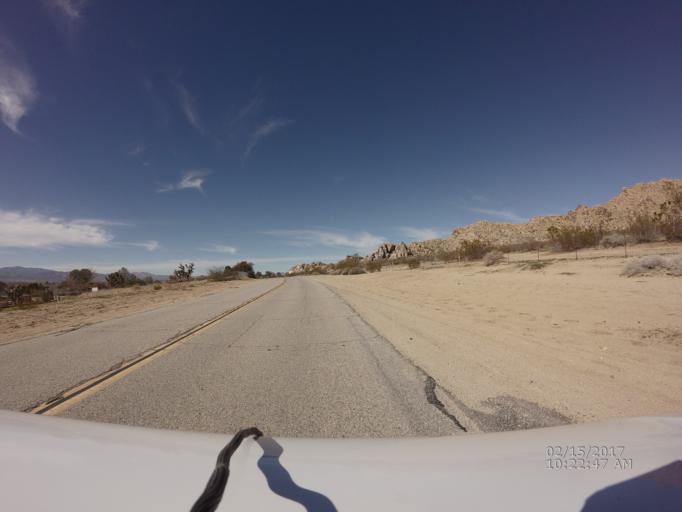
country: US
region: California
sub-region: Los Angeles County
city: Lake Los Angeles
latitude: 34.5872
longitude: -117.8494
